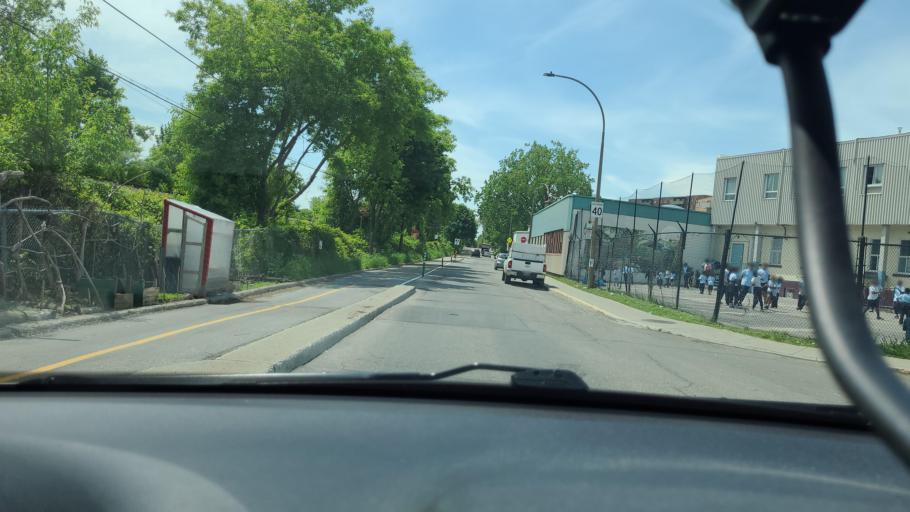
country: CA
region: Quebec
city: Saint-Raymond
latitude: 45.4639
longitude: -73.6225
